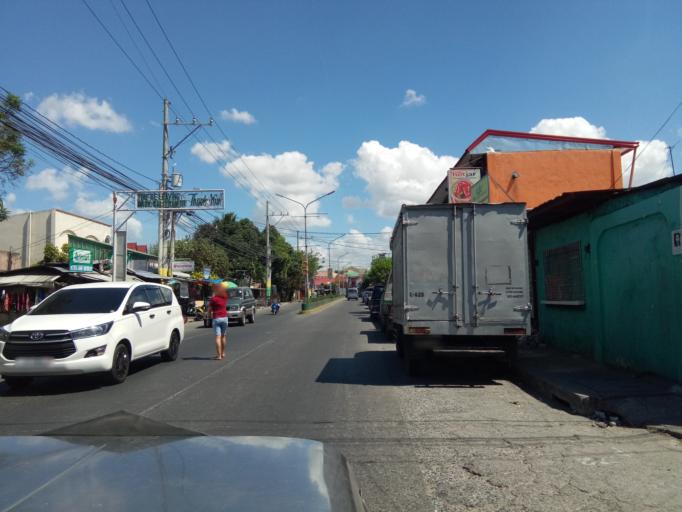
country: PH
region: Calabarzon
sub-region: Province of Cavite
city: Dasmarinas
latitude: 14.3416
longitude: 120.9481
